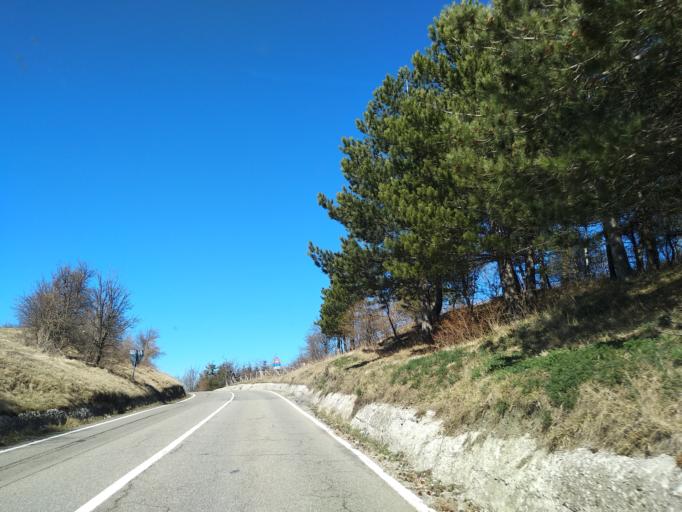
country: IT
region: Emilia-Romagna
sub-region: Provincia di Reggio Emilia
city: Busana
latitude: 44.4053
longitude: 10.3319
